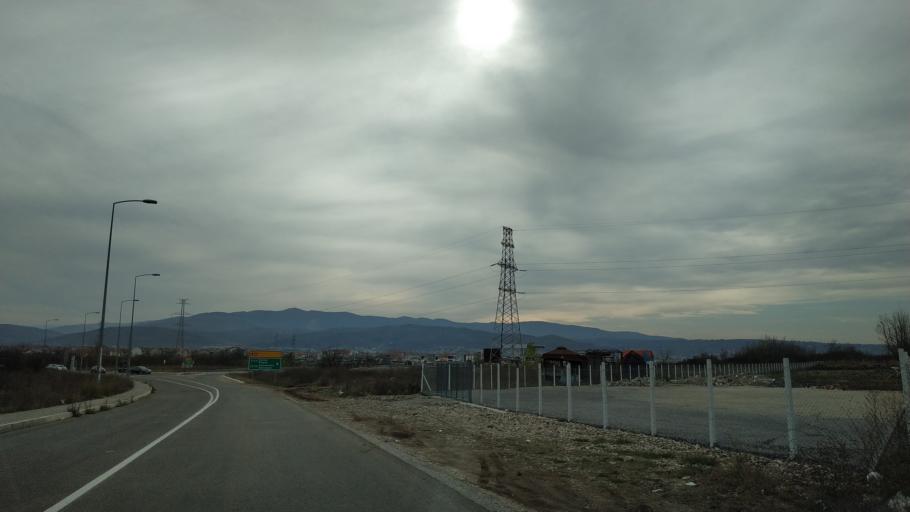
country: RS
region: Central Serbia
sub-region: Nisavski Okrug
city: Nis
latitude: 43.3443
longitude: 21.9367
